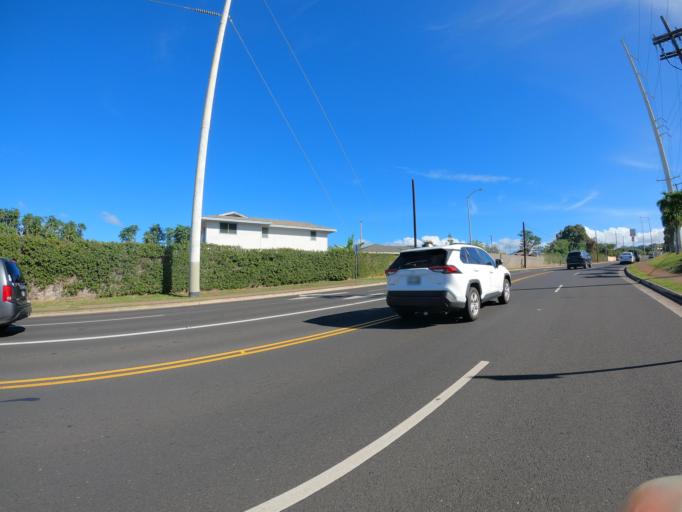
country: US
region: Hawaii
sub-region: Honolulu County
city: Halawa
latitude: 21.3583
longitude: -157.9265
